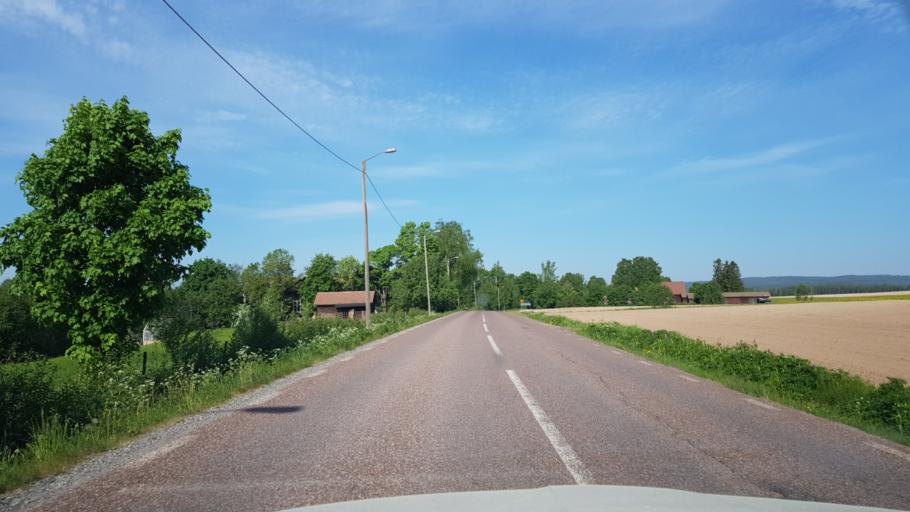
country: SE
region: Dalarna
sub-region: Saters Kommun
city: Saeter
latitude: 60.4139
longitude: 15.7760
